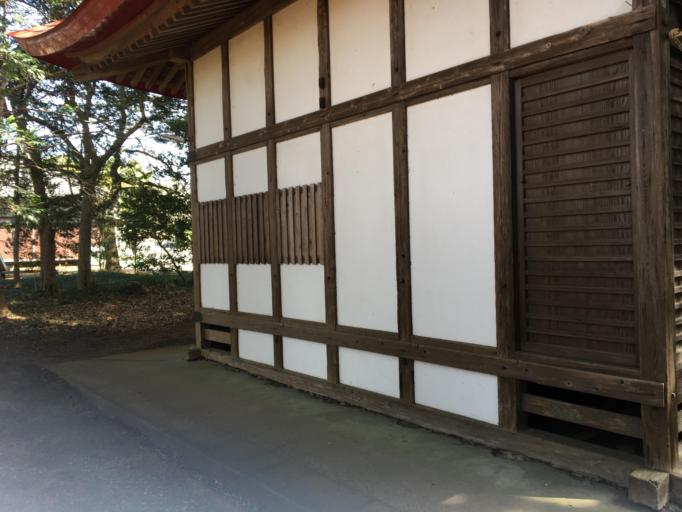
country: JP
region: Saitama
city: Sakado
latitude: 35.9917
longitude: 139.3358
